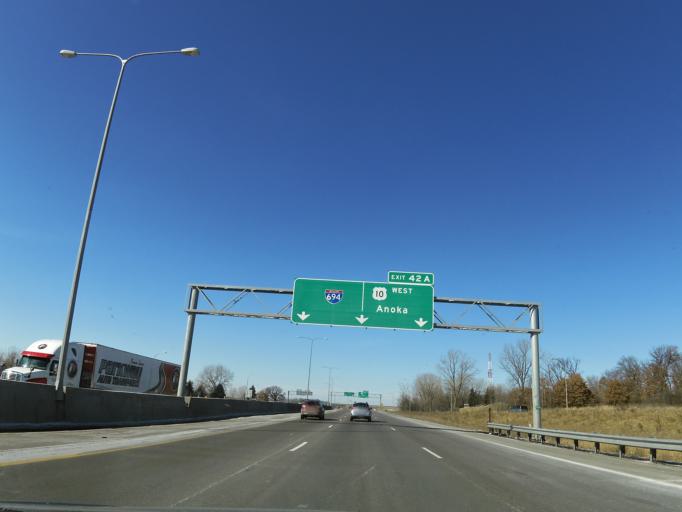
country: US
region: Minnesota
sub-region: Ramsey County
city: Arden Hills
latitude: 45.0600
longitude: -93.1481
